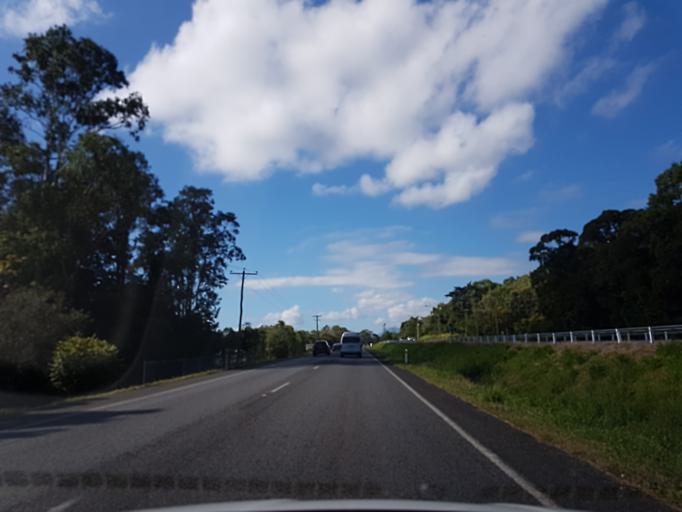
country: AU
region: Queensland
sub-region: Cairns
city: Trinity Beach
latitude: -16.7958
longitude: 145.6821
